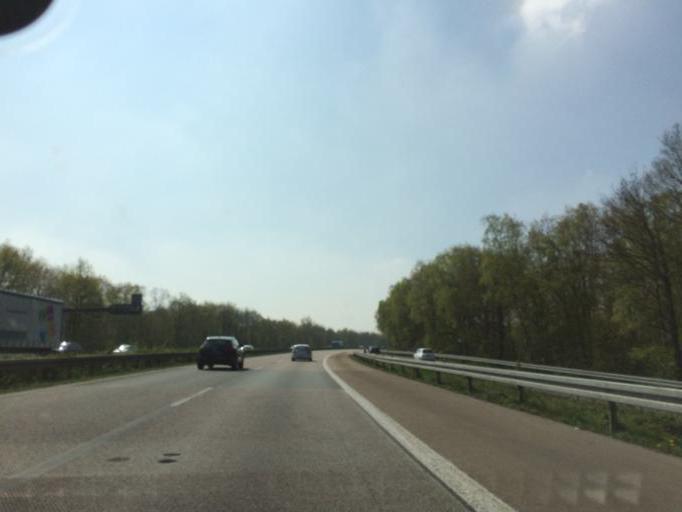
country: DE
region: North Rhine-Westphalia
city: Marl
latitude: 51.6778
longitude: 7.1224
